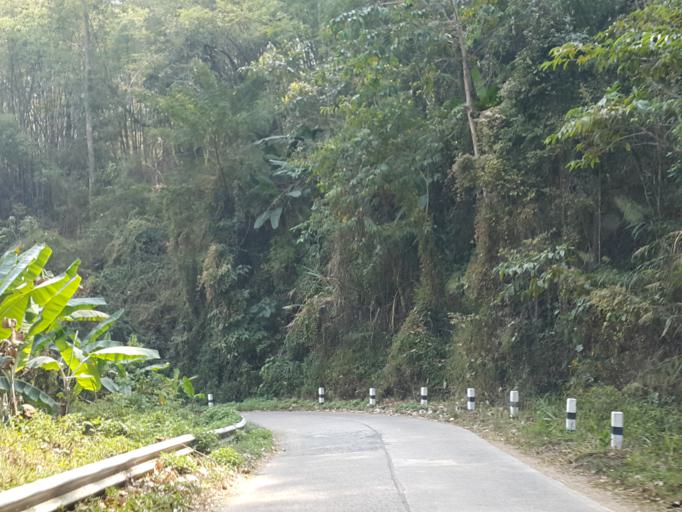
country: TH
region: Chiang Mai
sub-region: Amphoe Chiang Dao
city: Chiang Dao
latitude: 19.4129
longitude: 98.8567
